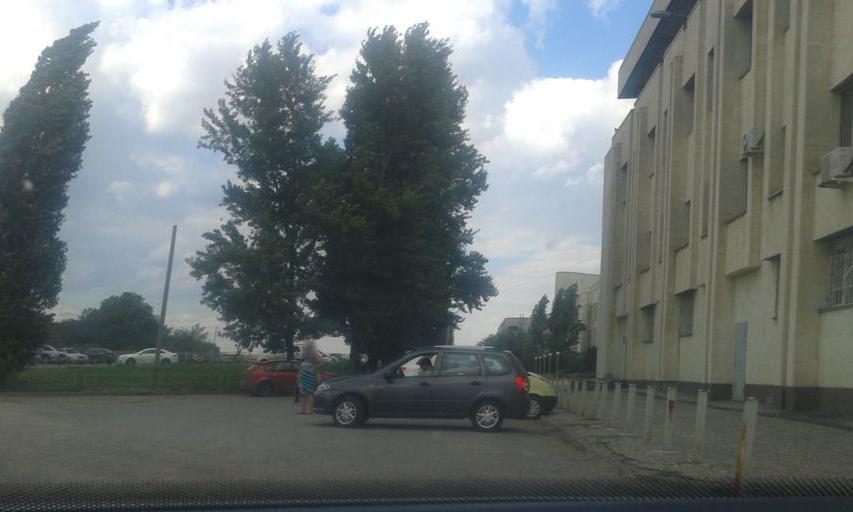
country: RU
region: Volgograd
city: Volgograd
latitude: 48.6410
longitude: 44.4210
